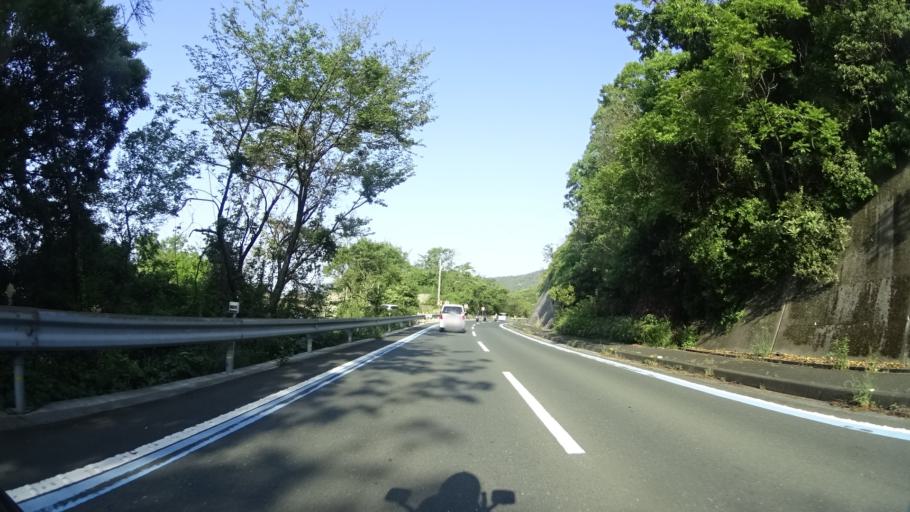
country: JP
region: Ehime
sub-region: Nishiuwa-gun
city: Ikata-cho
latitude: 33.4314
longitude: 132.2251
